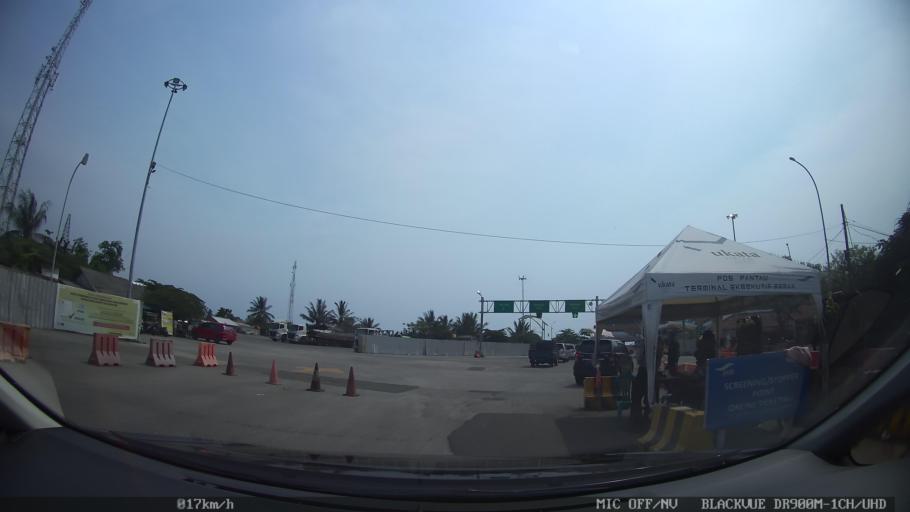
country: ID
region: Banten
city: Kubangkepuh
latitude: -5.9355
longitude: 106.0013
